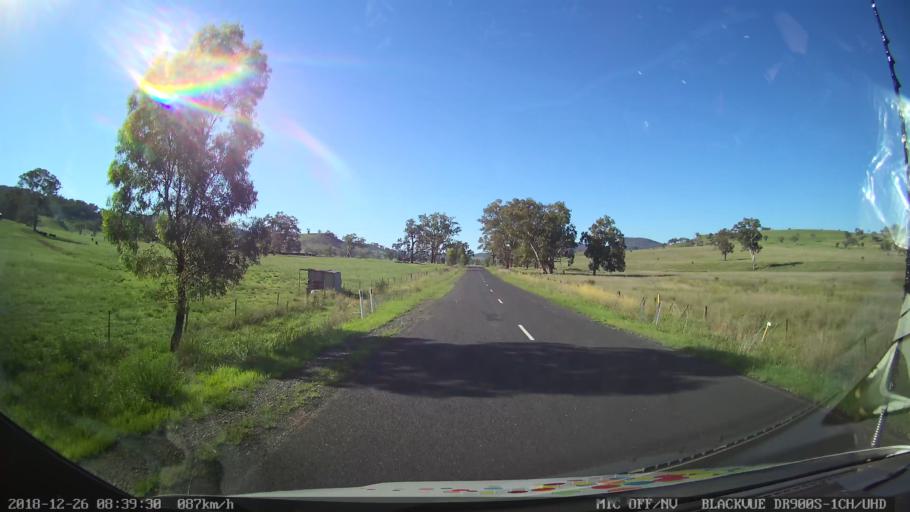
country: AU
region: New South Wales
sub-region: Mid-Western Regional
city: Kandos
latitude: -32.4543
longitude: 150.0756
